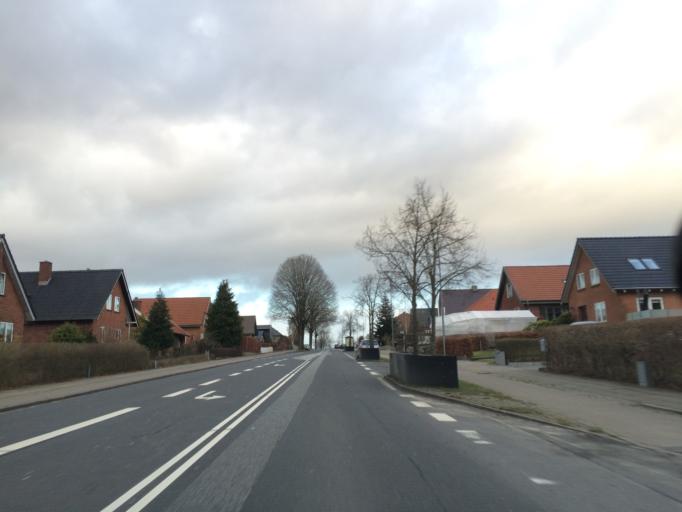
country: DK
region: Central Jutland
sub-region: Silkeborg Kommune
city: Silkeborg
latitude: 56.1570
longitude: 9.5494
